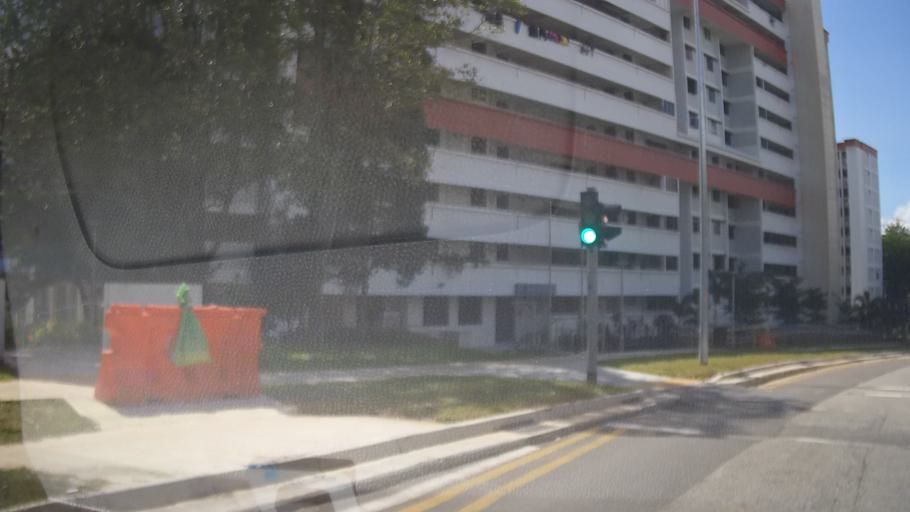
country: MY
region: Johor
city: Johor Bahru
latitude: 1.4360
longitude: 103.7807
